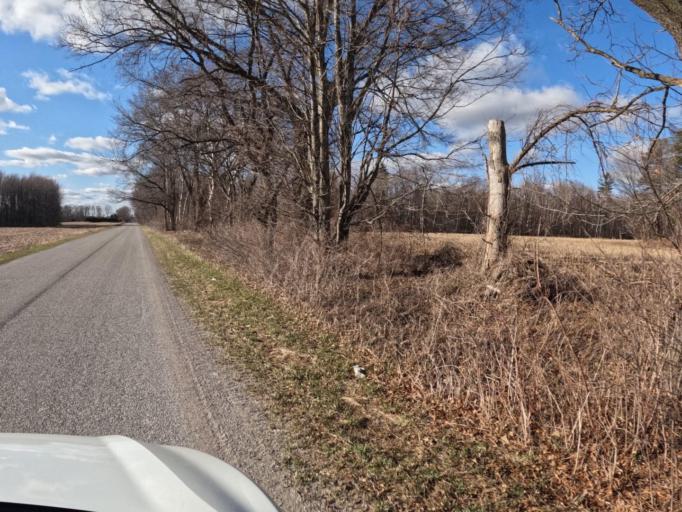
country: CA
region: Ontario
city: Norfolk County
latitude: 42.8174
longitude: -80.5668
